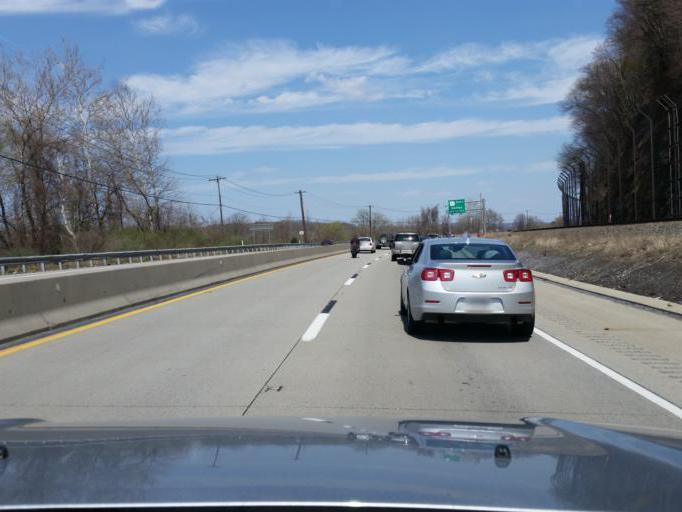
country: US
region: Pennsylvania
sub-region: Perry County
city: Duncannon
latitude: 40.3887
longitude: -77.0191
